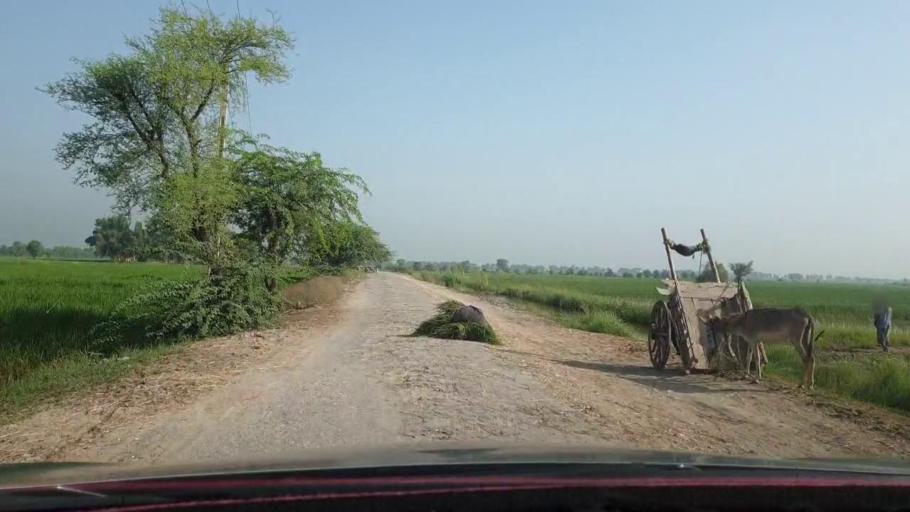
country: PK
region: Sindh
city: Nasirabad
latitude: 27.4392
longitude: 67.9206
